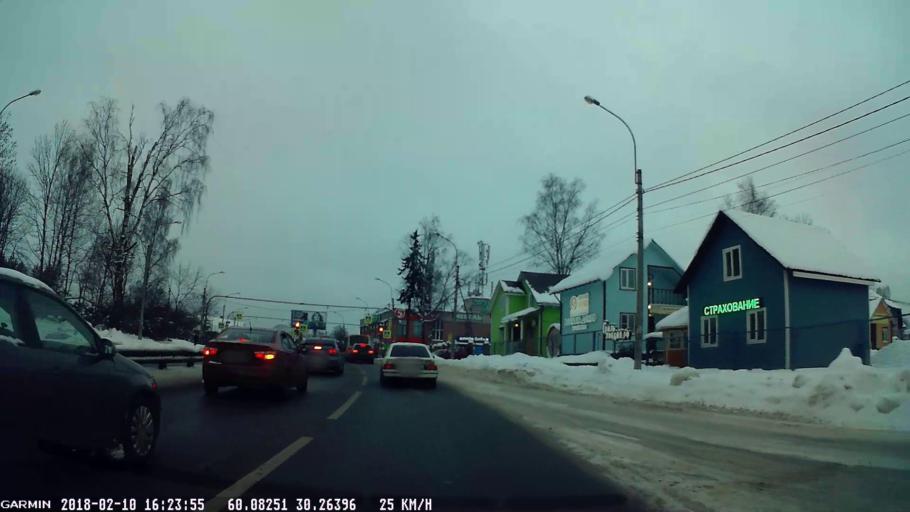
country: RU
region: St.-Petersburg
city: Pargolovo
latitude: 60.0829
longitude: 30.2637
